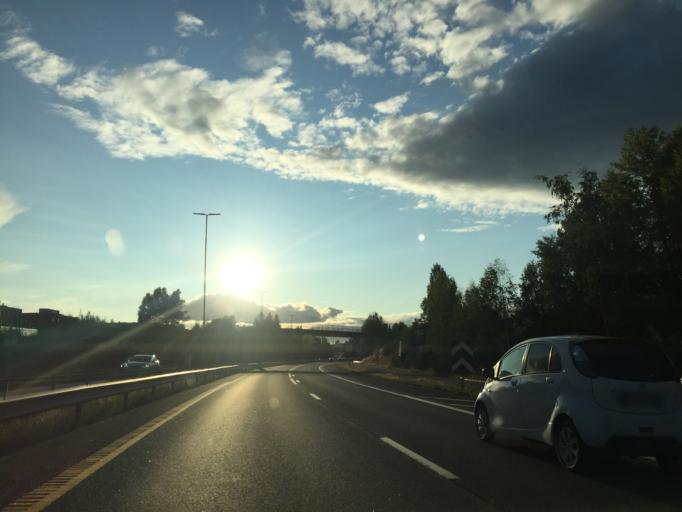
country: NO
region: Akershus
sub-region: Lorenskog
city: Kjenn
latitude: 59.9286
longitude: 10.9561
